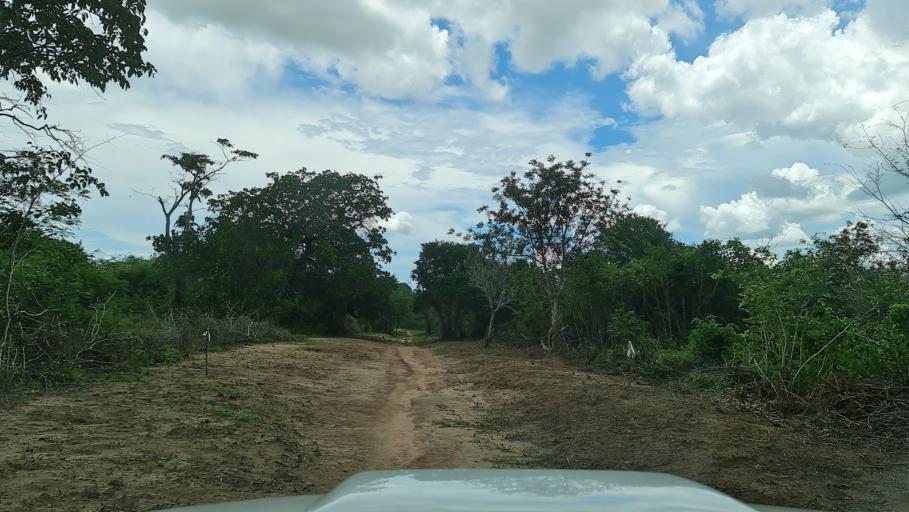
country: MZ
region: Nampula
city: Ilha de Mocambique
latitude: -15.5004
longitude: 40.1731
